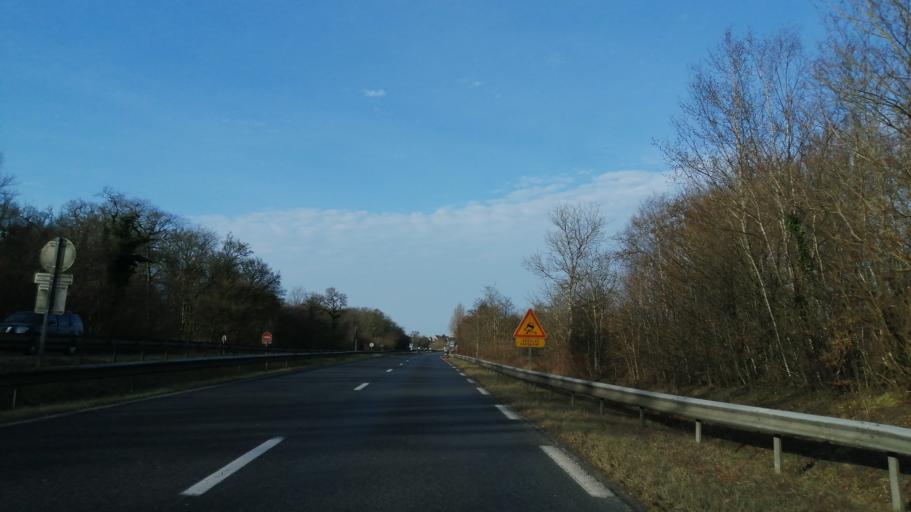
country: FR
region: Nord-Pas-de-Calais
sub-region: Departement du Pas-de-Calais
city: La Capelle-les-Boulogne
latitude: 50.7328
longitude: 1.7250
